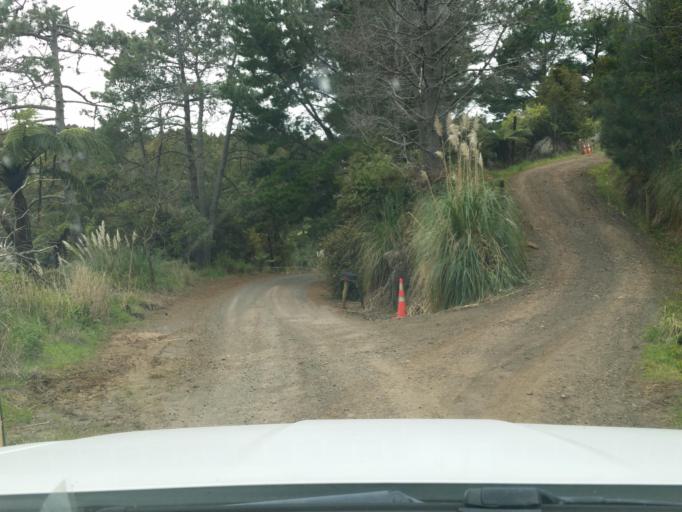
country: NZ
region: Northland
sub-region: Kaipara District
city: Dargaville
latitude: -35.7091
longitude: 173.6231
